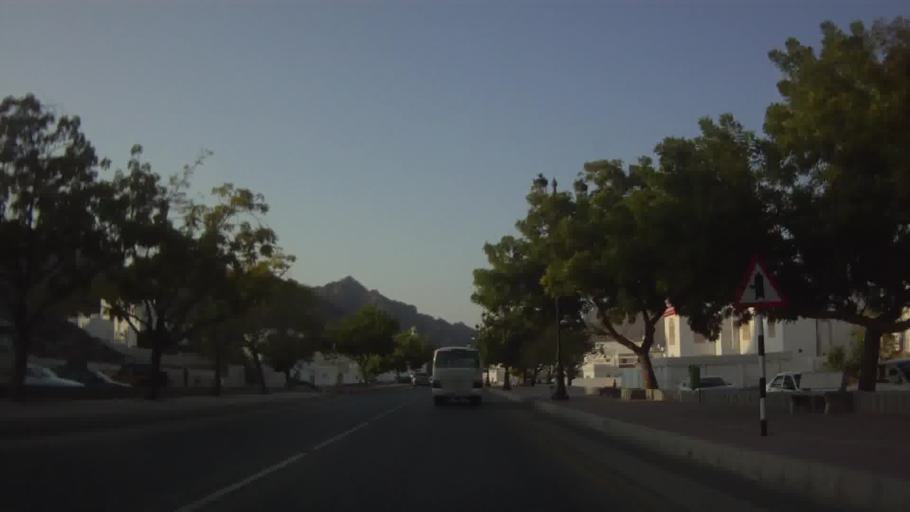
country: OM
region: Muhafazat Masqat
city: Muscat
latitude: 23.5940
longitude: 58.5981
